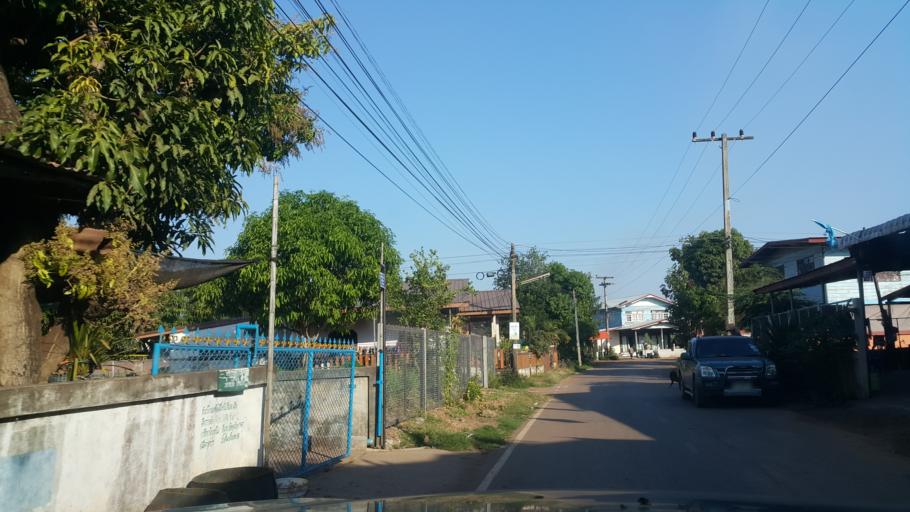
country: TH
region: Changwat Udon Thani
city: Ban Na Muang
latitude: 17.2390
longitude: 103.0677
